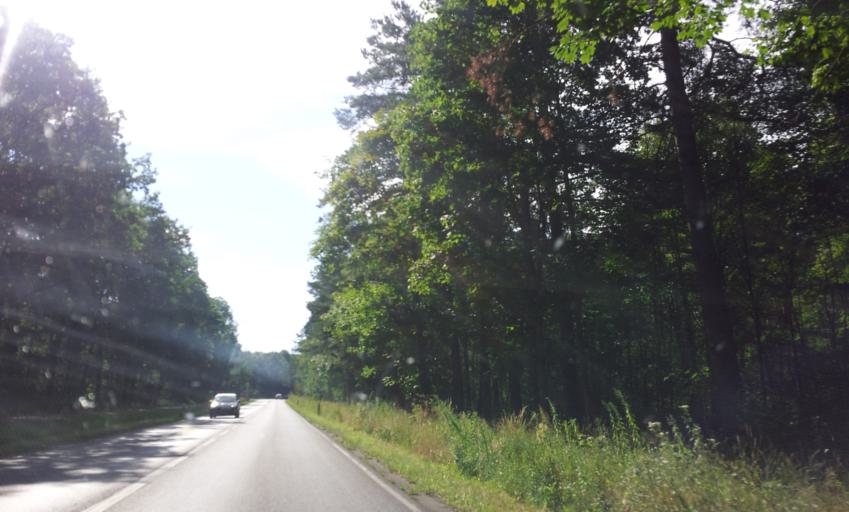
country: DE
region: Berlin
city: Friedrichshagen
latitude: 52.4313
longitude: 13.6117
